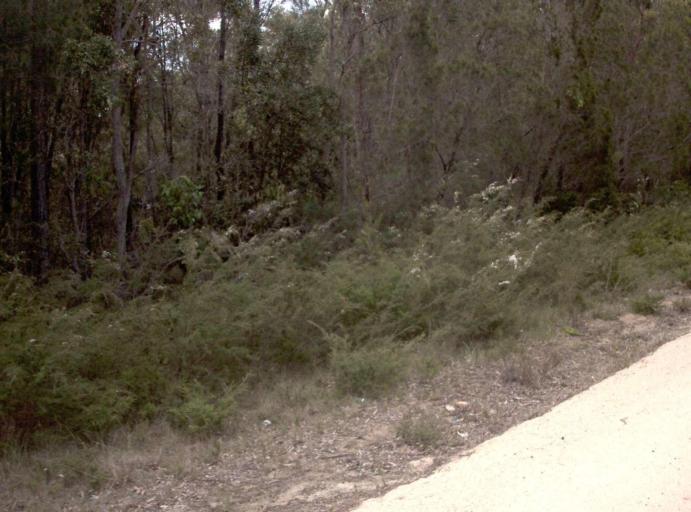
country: AU
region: New South Wales
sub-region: Bega Valley
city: Eden
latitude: -37.4244
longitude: 149.6460
